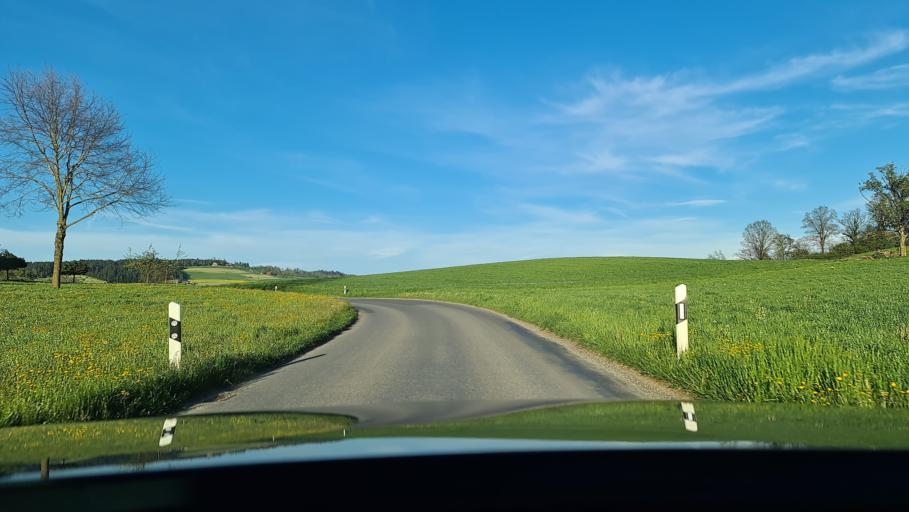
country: CH
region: Lucerne
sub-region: Entlebuch District
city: Wolhusen
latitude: 47.0837
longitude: 8.0904
